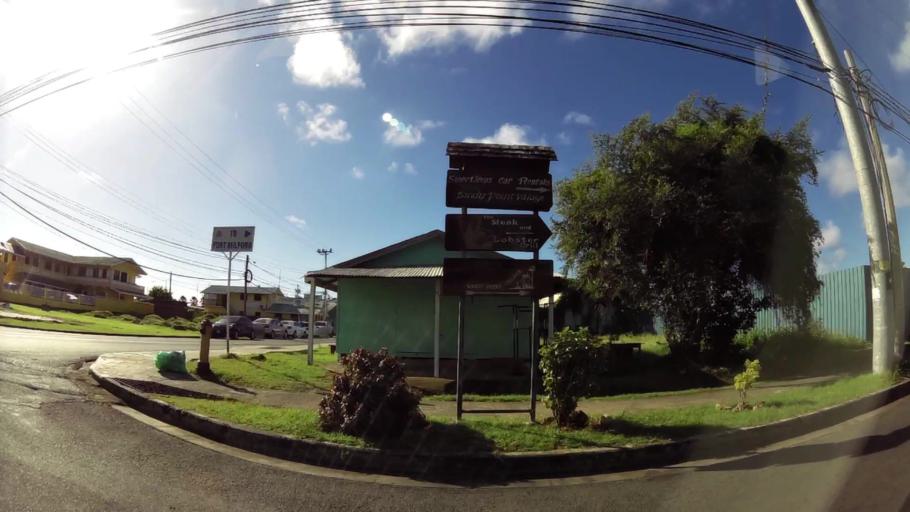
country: TT
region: Tobago
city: Scarborough
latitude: 11.1539
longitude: -60.8401
